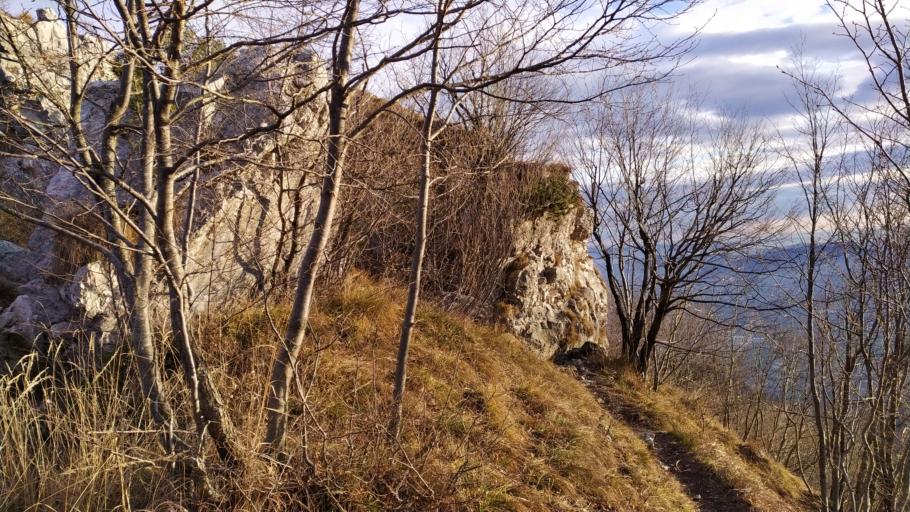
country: IT
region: Veneto
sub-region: Provincia di Vicenza
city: Velo d'Astico
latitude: 45.7663
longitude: 11.3719
